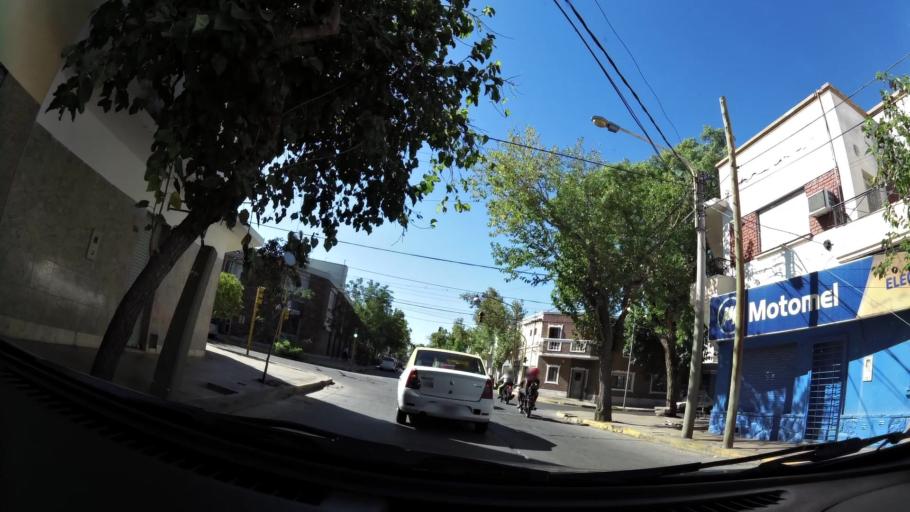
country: AR
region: San Juan
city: San Juan
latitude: -31.5437
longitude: -68.5343
